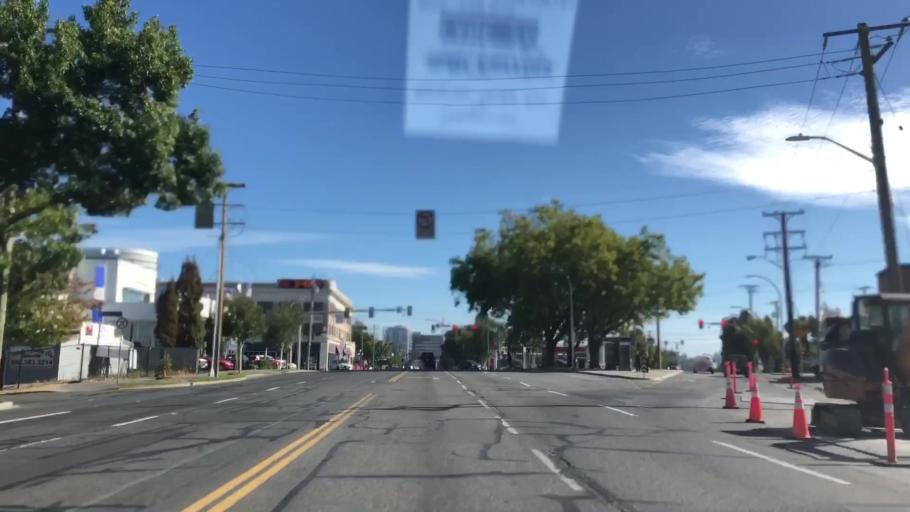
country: CA
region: British Columbia
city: Victoria
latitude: 48.4393
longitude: -123.3675
